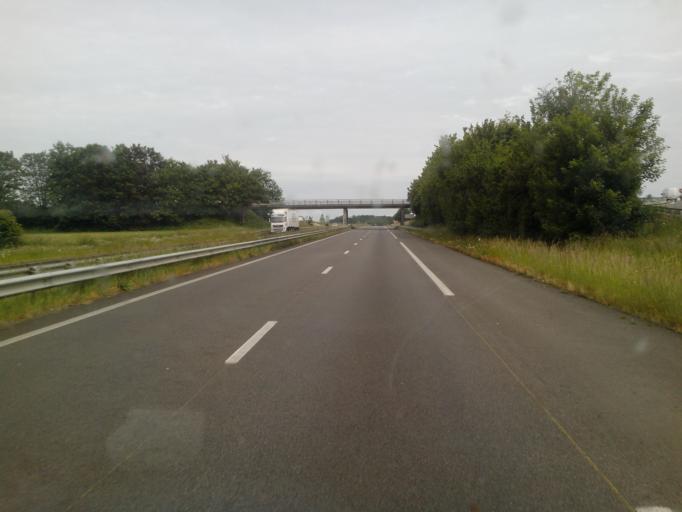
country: FR
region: Brittany
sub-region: Departement d'Ille-et-Vilaine
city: Montauban-de-Bretagne
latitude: 48.1951
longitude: -2.0251
